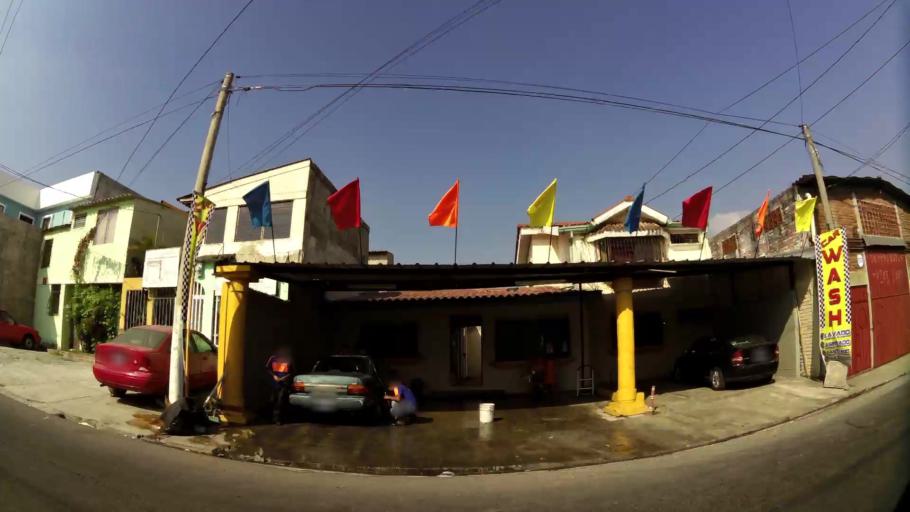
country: SV
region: La Libertad
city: Antiguo Cuscatlan
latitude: 13.6767
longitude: -89.2358
